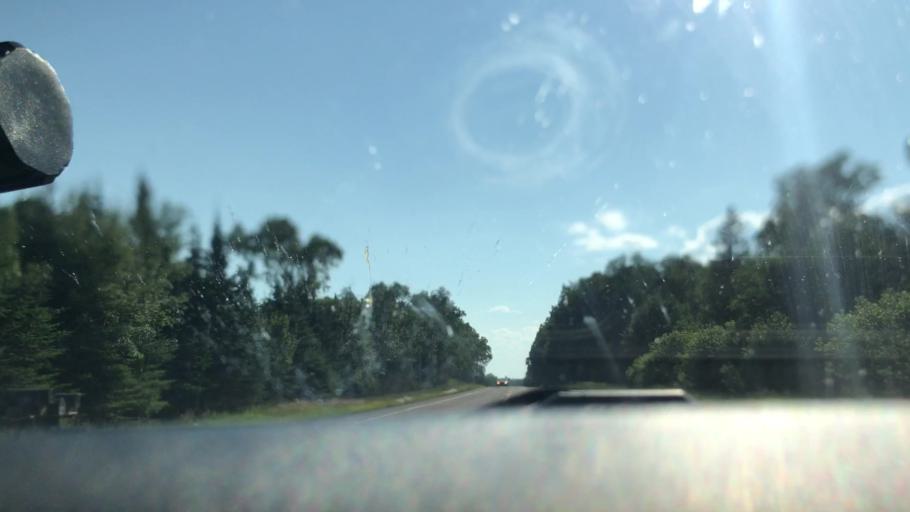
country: US
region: Minnesota
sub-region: Cook County
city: Grand Marais
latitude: 47.8207
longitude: -90.0408
